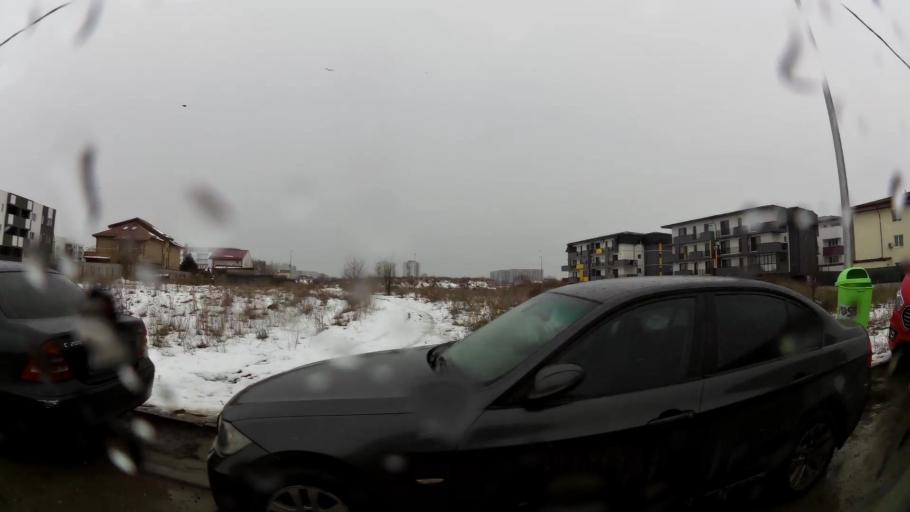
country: RO
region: Ilfov
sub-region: Comuna Glina
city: Catelu
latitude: 44.4177
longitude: 26.1908
